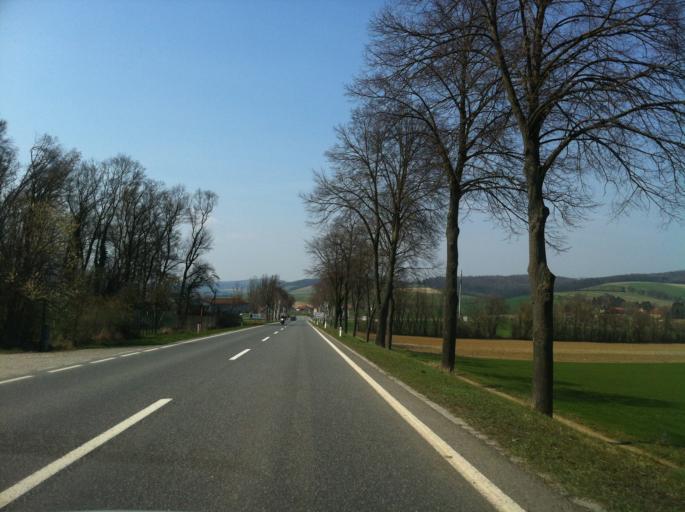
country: AT
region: Lower Austria
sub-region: Politischer Bezirk Tulln
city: Tulbing
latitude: 48.2560
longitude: 16.0816
